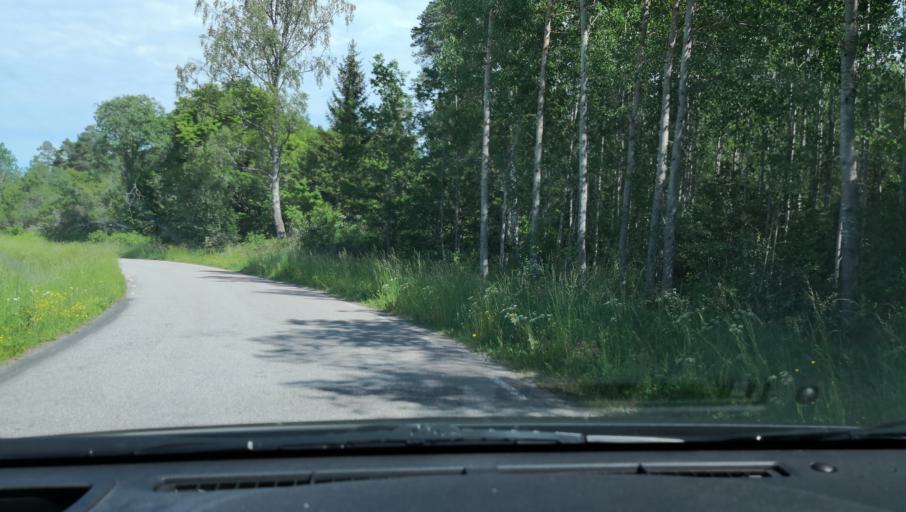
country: SE
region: Uppsala
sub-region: Uppsala Kommun
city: Alsike
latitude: 59.7051
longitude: 17.6679
